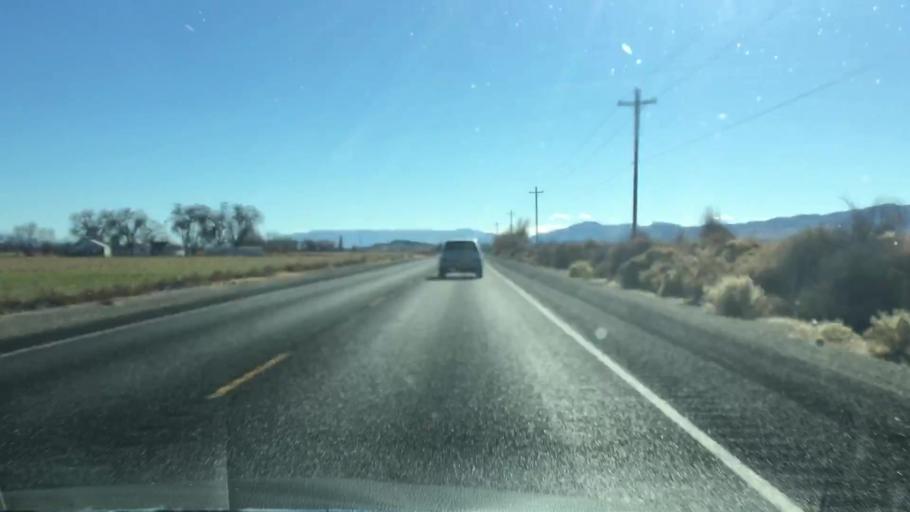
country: US
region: Nevada
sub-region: Lyon County
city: Yerington
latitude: 39.0652
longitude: -119.1813
